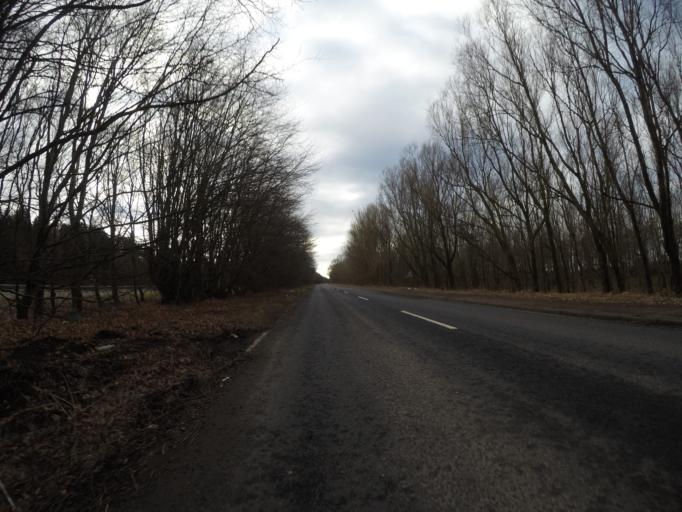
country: GB
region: Scotland
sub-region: North Ayrshire
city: Dreghorn
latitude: 55.5839
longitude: -4.6461
